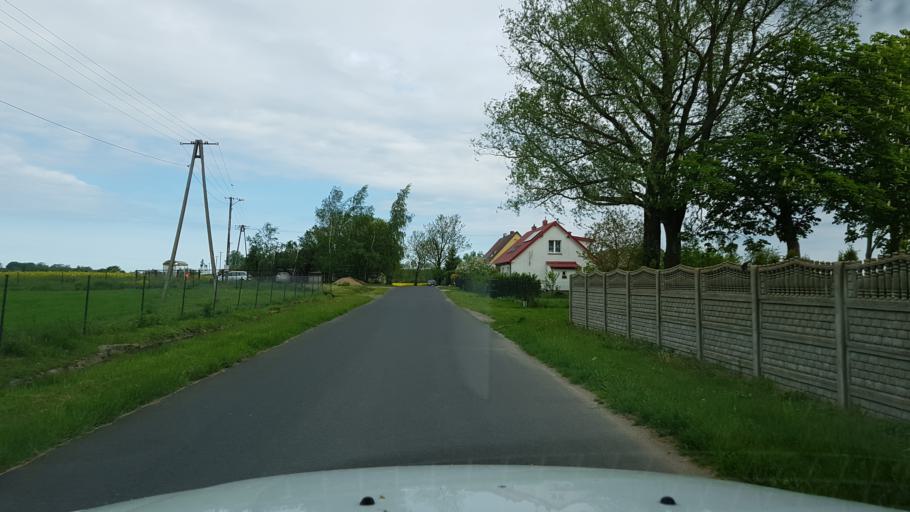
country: PL
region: West Pomeranian Voivodeship
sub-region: Powiat kolobrzeski
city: Ustronie Morskie
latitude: 54.2141
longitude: 15.8203
